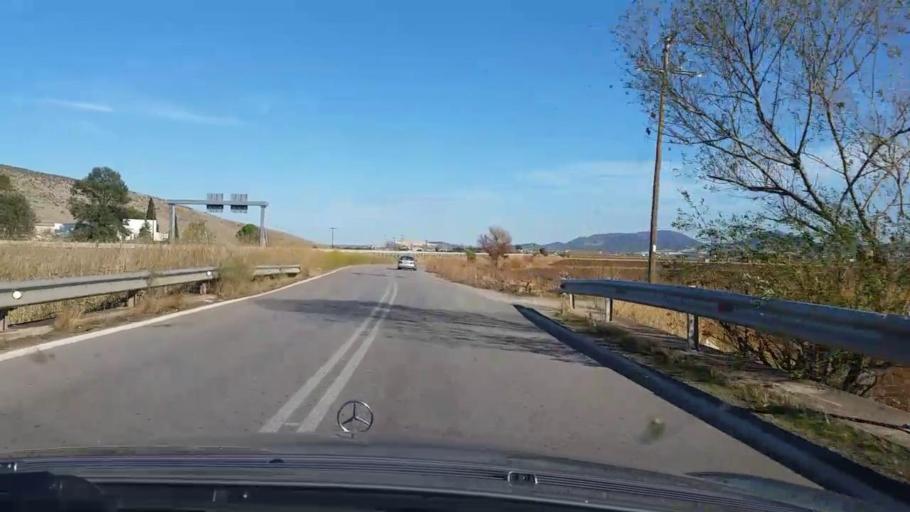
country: GR
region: Central Greece
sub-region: Nomos Voiotias
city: Thivai
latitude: 38.3698
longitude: 23.2897
